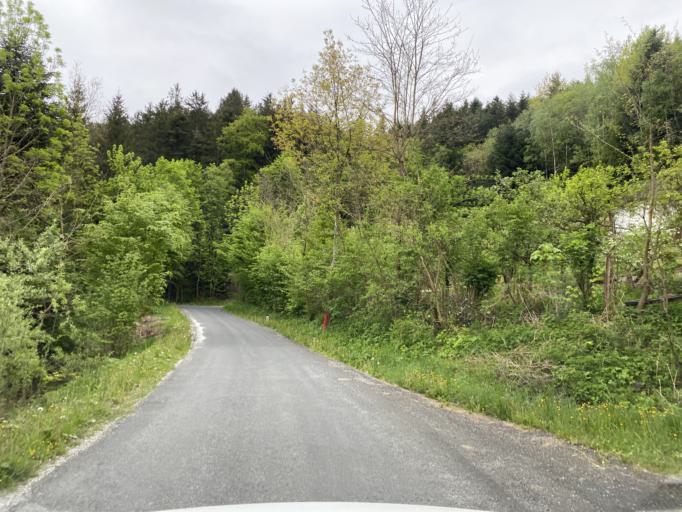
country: AT
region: Styria
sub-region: Politischer Bezirk Weiz
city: Koglhof
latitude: 47.3114
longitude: 15.6867
